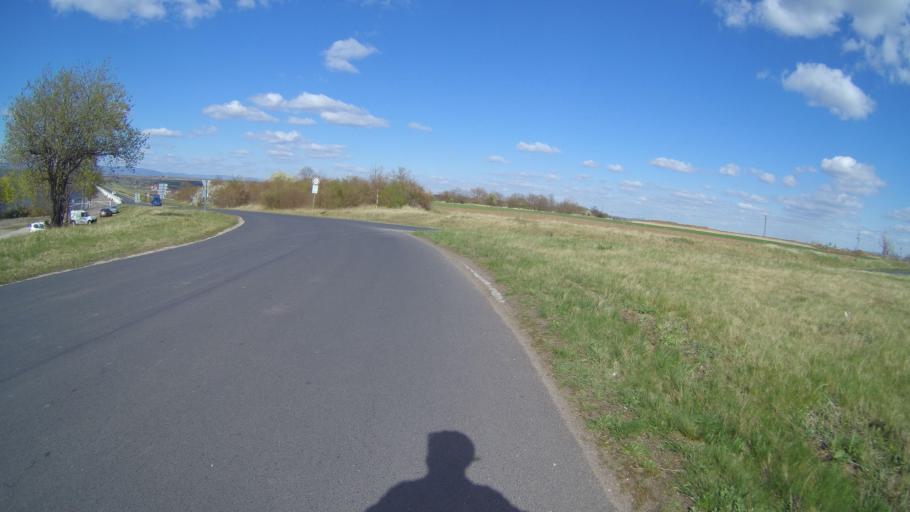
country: CZ
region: Ustecky
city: Brezno
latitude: 50.3467
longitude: 13.4146
